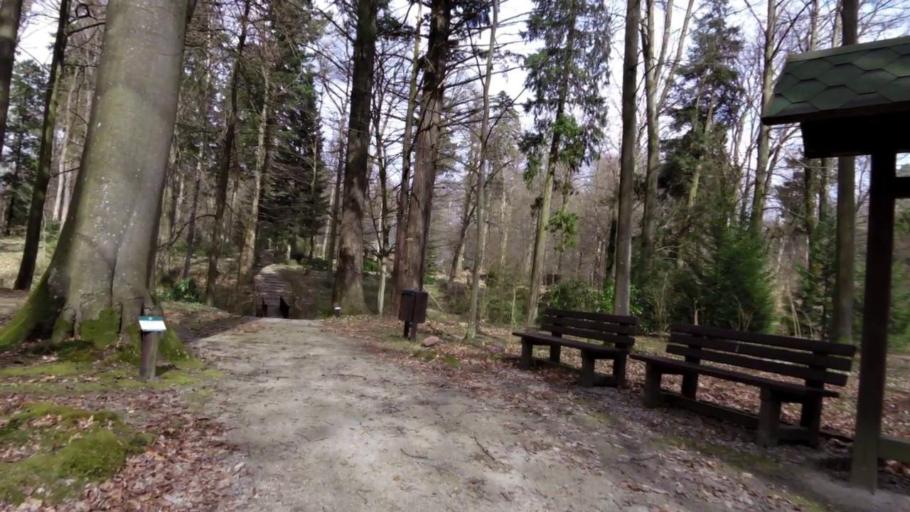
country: PL
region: West Pomeranian Voivodeship
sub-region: Powiat koszalinski
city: Sianow
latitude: 54.2694
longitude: 16.3274
